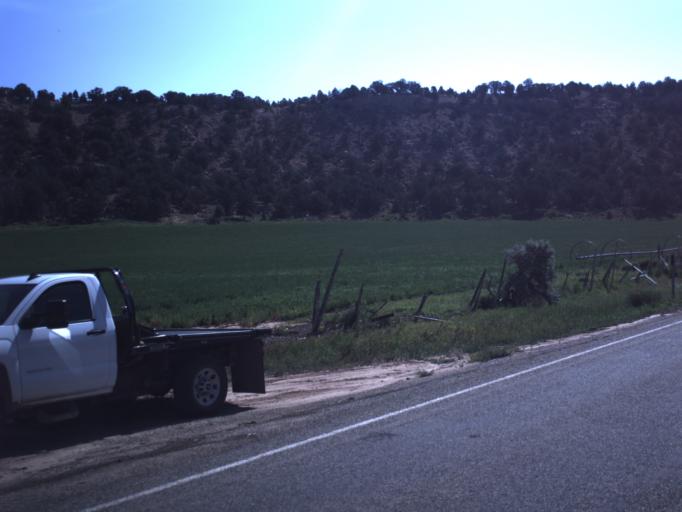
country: US
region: Utah
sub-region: Duchesne County
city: Duchesne
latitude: 40.3332
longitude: -110.6750
